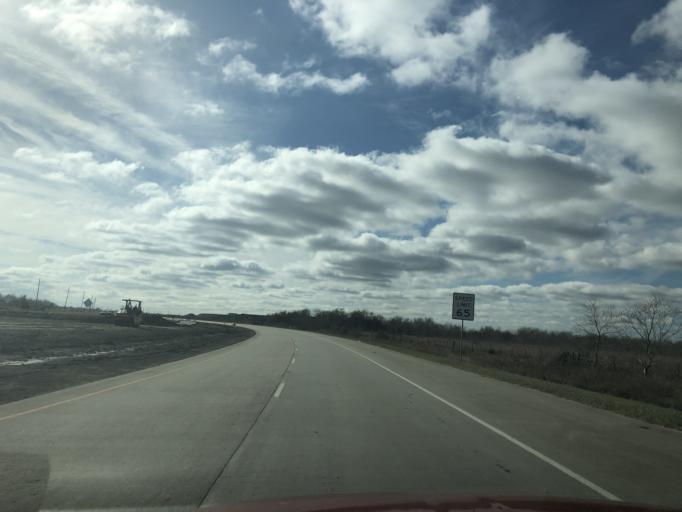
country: US
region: Texas
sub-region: Chambers County
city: Mont Belvieu
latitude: 29.8028
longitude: -94.8690
